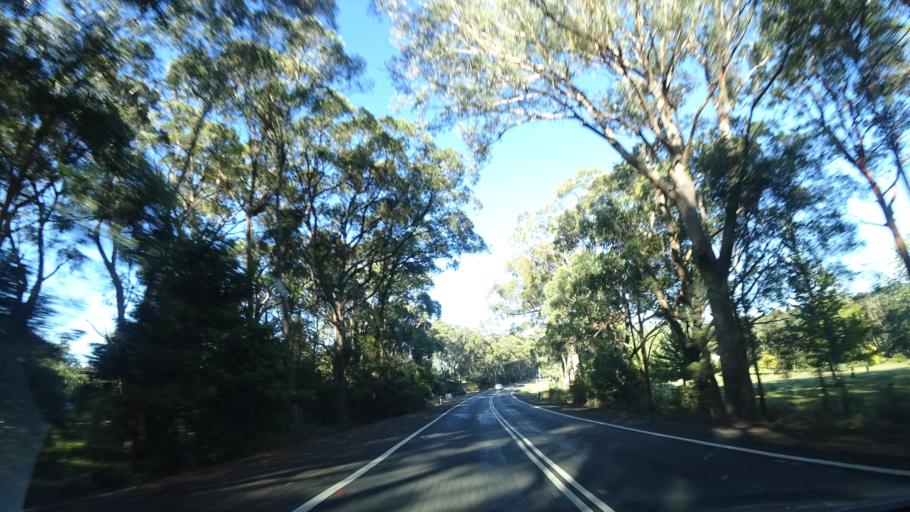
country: AU
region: New South Wales
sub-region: Blue Mountains Municipality
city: Hazelbrook
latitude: -33.5165
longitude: 150.4861
